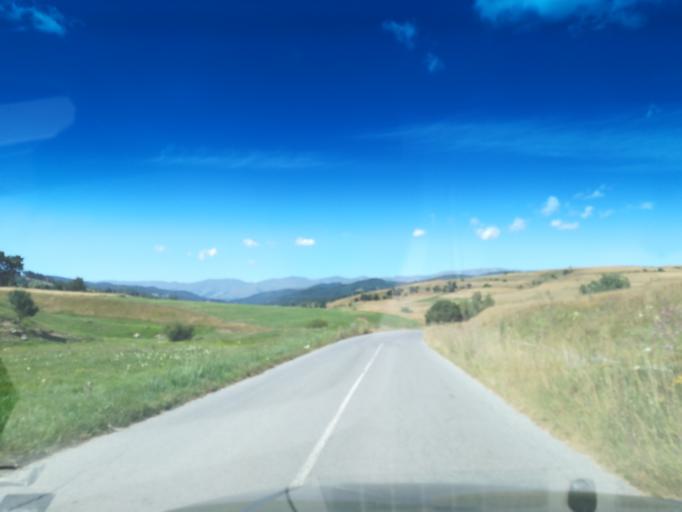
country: BG
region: Sofiya
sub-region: Obshtina Koprivshtitsa
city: Koprivshtitsa
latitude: 42.6002
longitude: 24.3795
